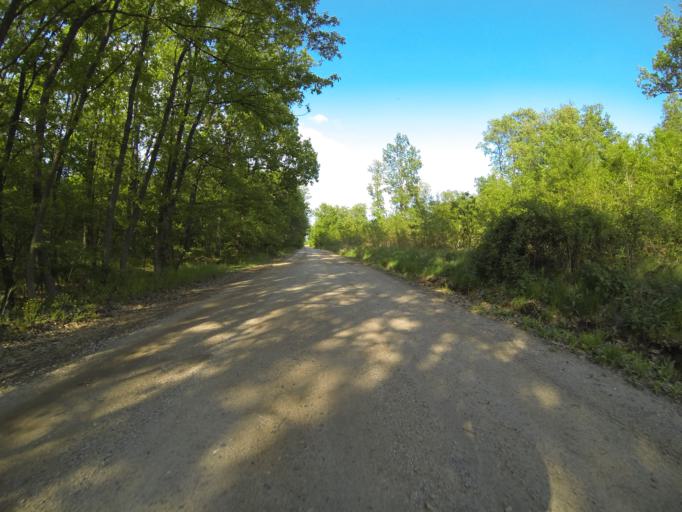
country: RO
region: Dolj
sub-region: Comuna Verbita
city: Verbita
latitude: 44.2900
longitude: 23.2056
